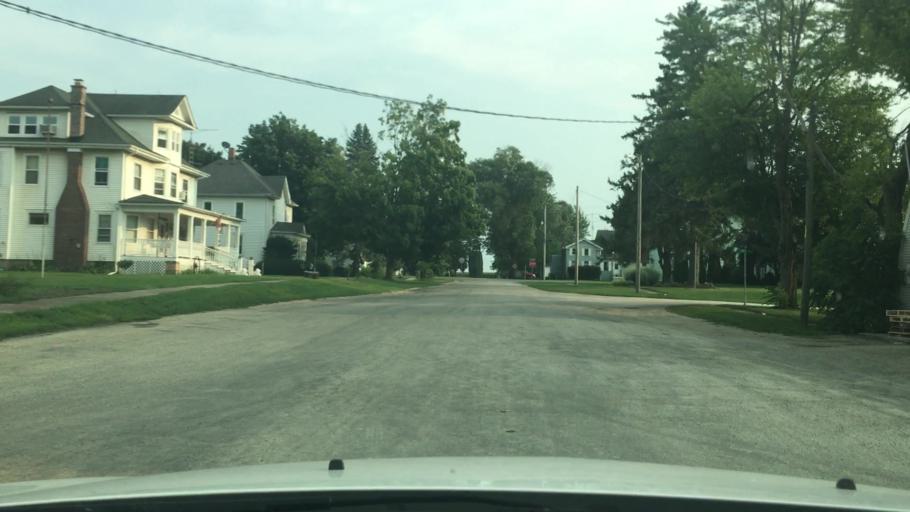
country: US
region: Illinois
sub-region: Ogle County
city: Hillcrest
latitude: 41.9299
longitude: -88.9648
